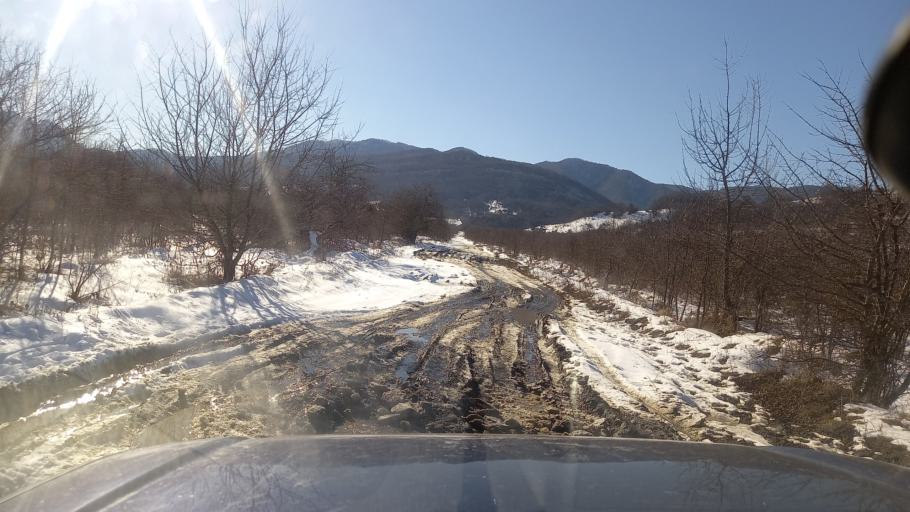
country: RU
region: Adygeya
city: Kamennomostskiy
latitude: 44.2099
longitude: 40.1629
